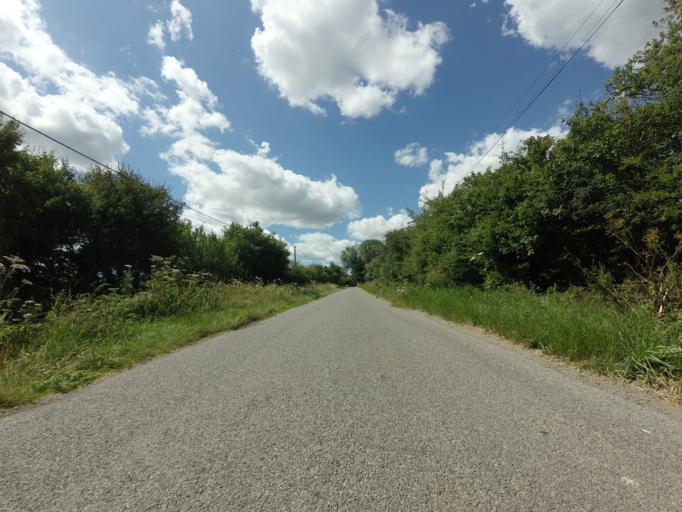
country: GB
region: England
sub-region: East Sussex
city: Hailsham
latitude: 50.8689
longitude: 0.1652
